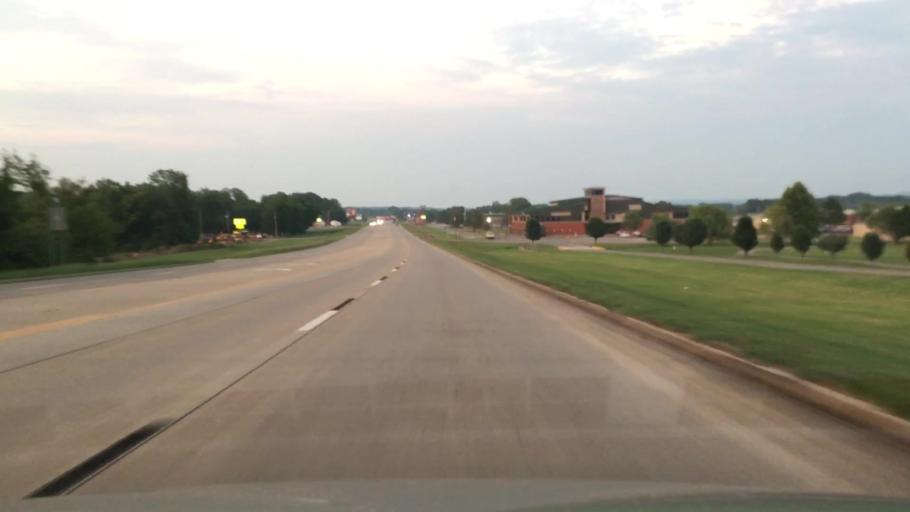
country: US
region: Oklahoma
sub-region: Cherokee County
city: Park Hill
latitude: 35.8515
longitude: -94.9953
